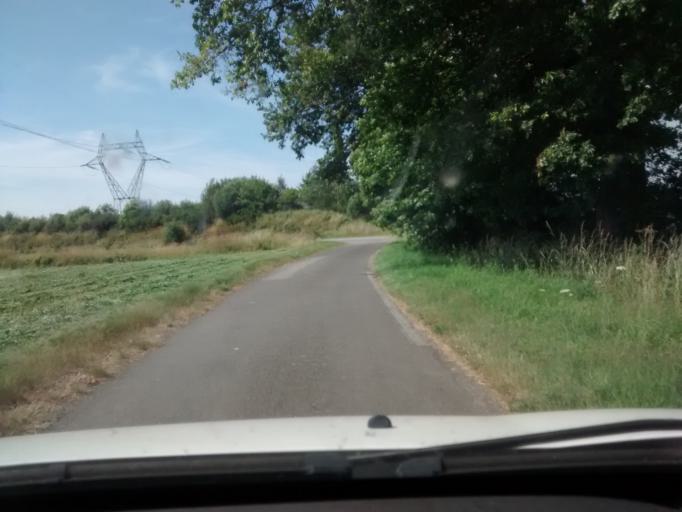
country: FR
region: Brittany
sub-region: Departement d'Ille-et-Vilaine
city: Acigne
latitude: 48.1135
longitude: -1.5592
